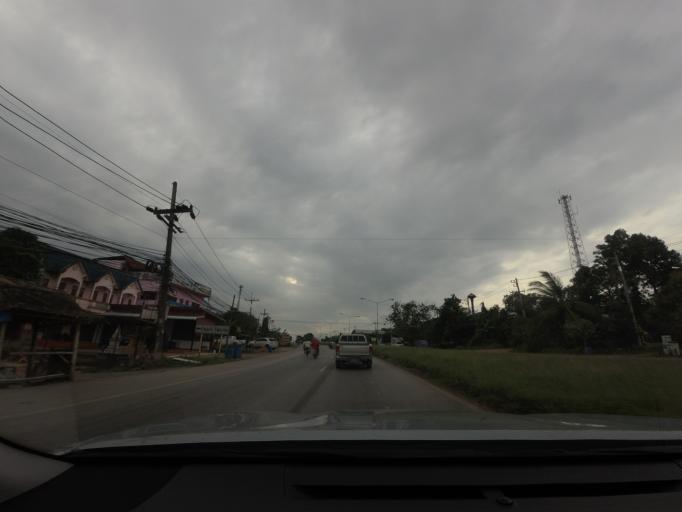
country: TH
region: Surat Thani
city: Phunphin
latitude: 9.0532
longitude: 99.1696
